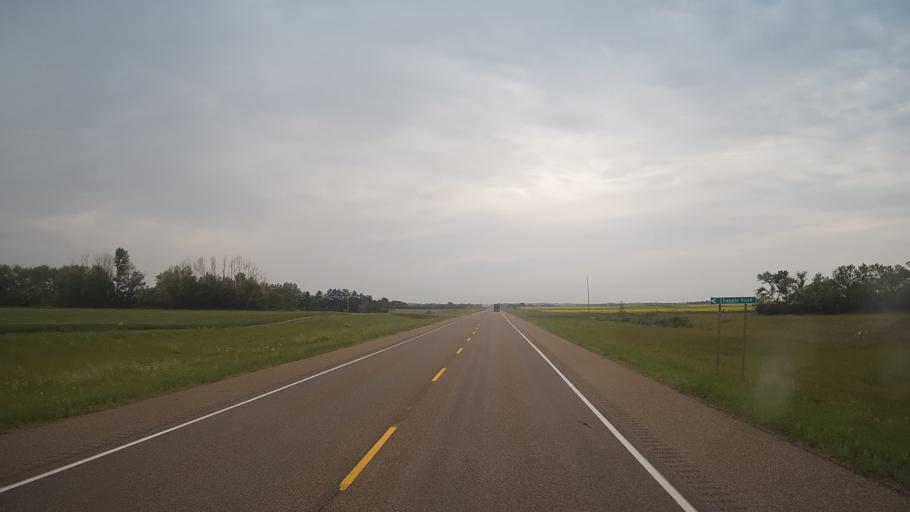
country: CA
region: Saskatchewan
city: Langham
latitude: 52.1294
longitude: -107.0714
